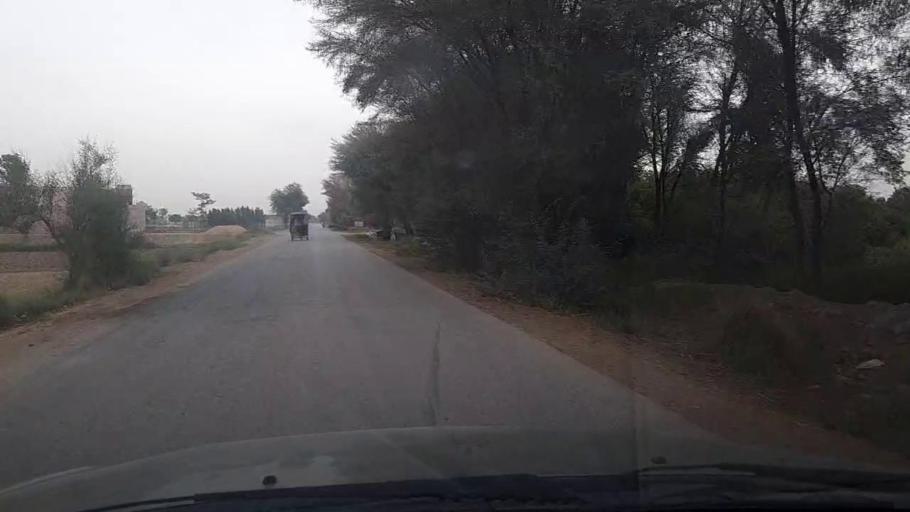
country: PK
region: Sindh
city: Daulatpur
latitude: 26.3203
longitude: 68.1050
